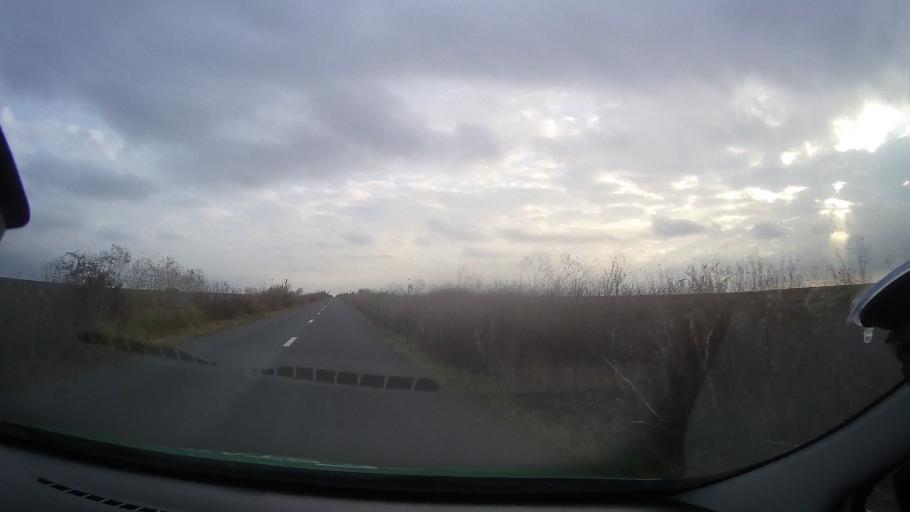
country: RO
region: Constanta
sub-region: Comuna Pestera
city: Pestera
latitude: 44.1447
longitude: 28.1158
